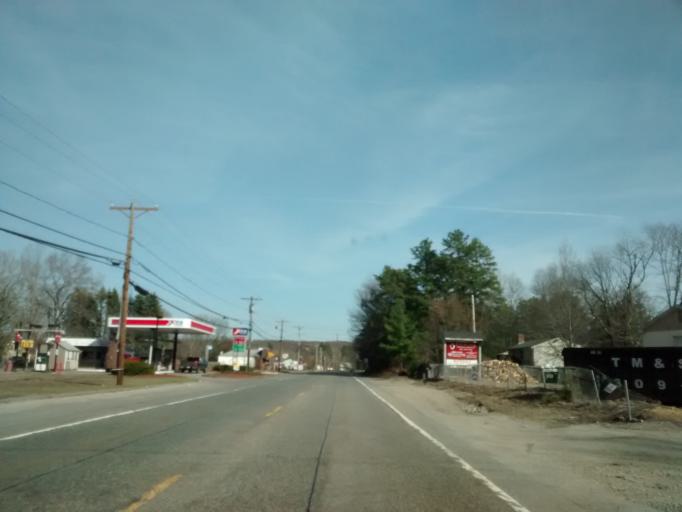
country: US
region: Massachusetts
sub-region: Worcester County
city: Millville
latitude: 42.0315
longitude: -71.6131
